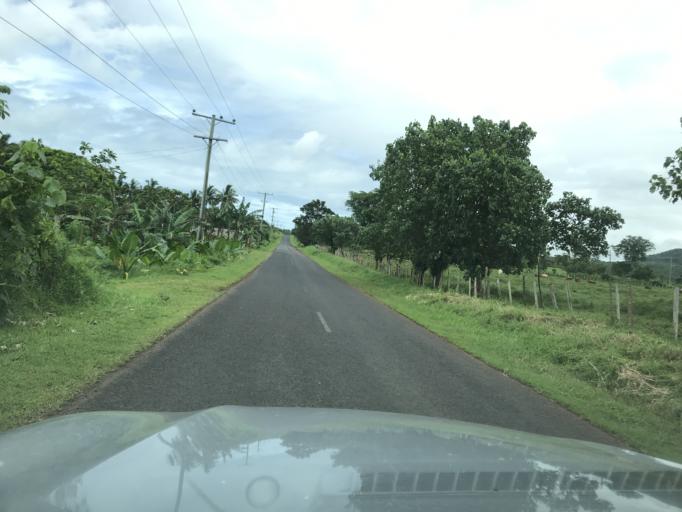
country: WS
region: A'ana
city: Leulumoega
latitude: -13.8766
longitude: -171.9352
